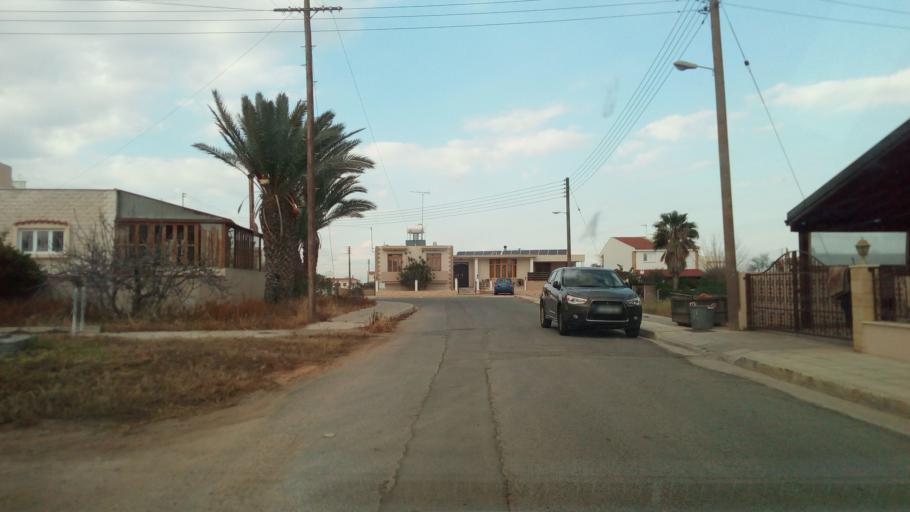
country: CY
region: Larnaka
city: Xylotymbou
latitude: 35.0202
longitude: 33.7455
